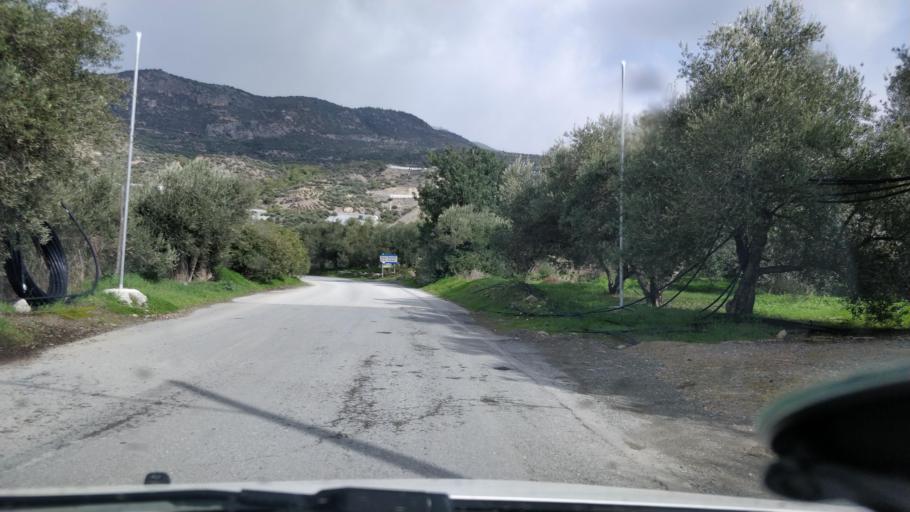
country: GR
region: Crete
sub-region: Nomos Lasithiou
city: Gra Liyia
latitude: 34.9927
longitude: 25.5040
